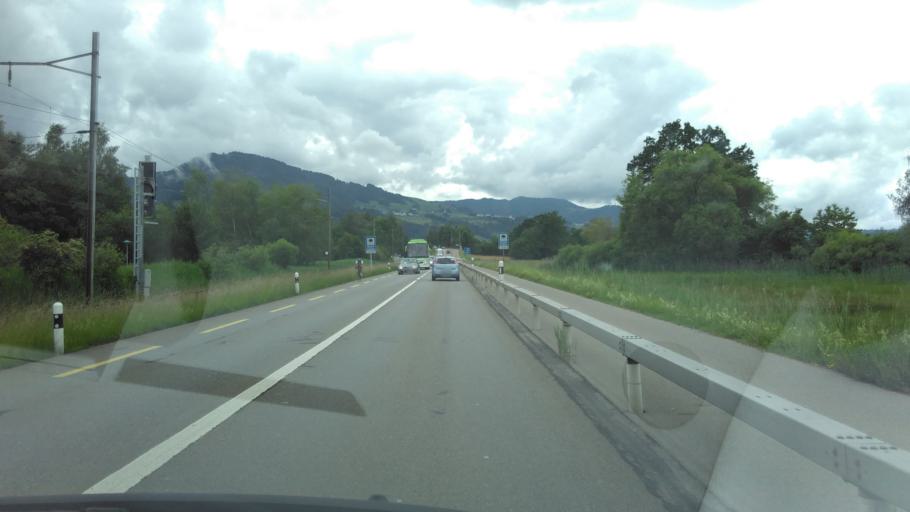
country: CH
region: Saint Gallen
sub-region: Wahlkreis See-Gaster
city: Rapperswil
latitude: 47.2168
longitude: 8.8046
